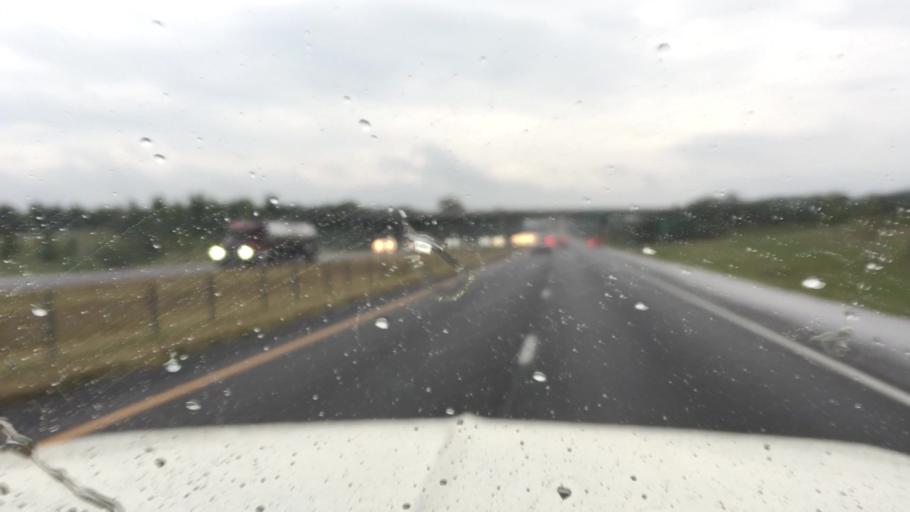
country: US
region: Alabama
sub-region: Morgan County
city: Hartselle
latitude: 34.4142
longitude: -86.8986
